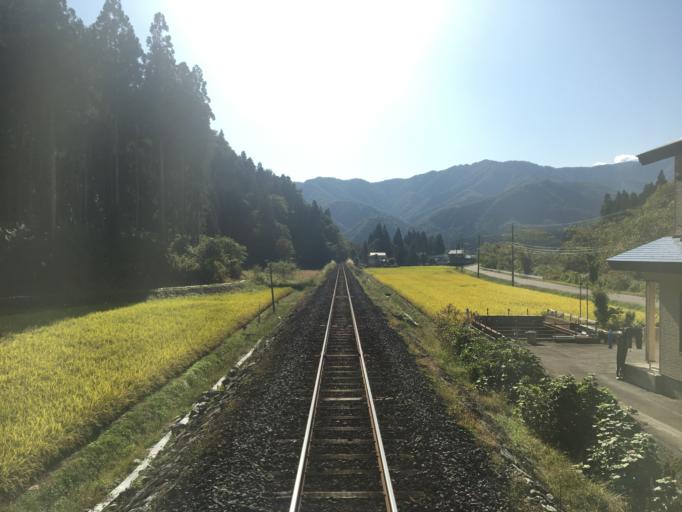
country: JP
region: Akita
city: Kakunodatemachi
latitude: 39.7307
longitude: 140.5731
